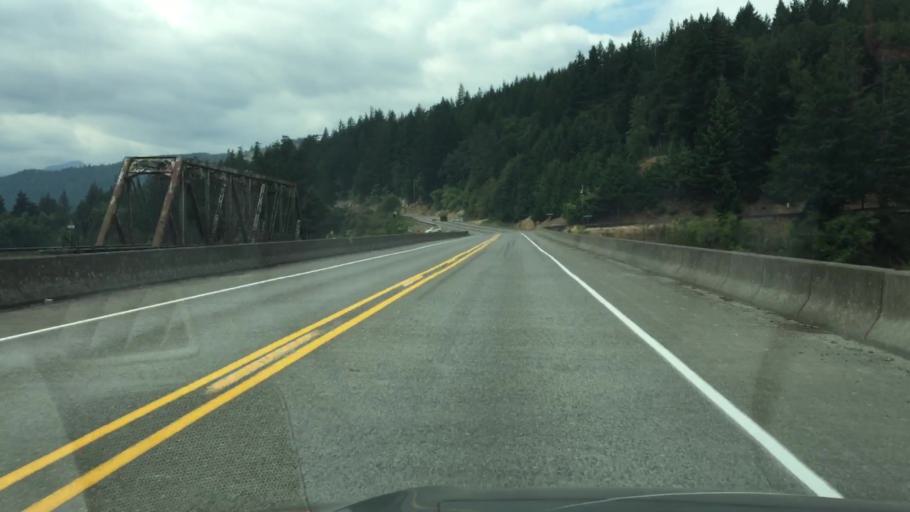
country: US
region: Washington
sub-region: Skamania County
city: Carson
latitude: 45.7155
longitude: -121.7905
